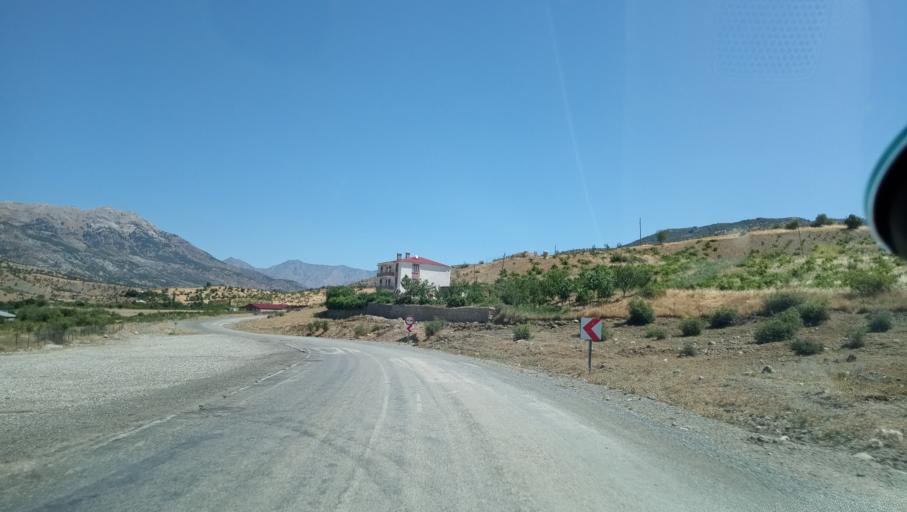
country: TR
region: Diyarbakir
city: Kulp
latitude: 38.4927
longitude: 41.0441
